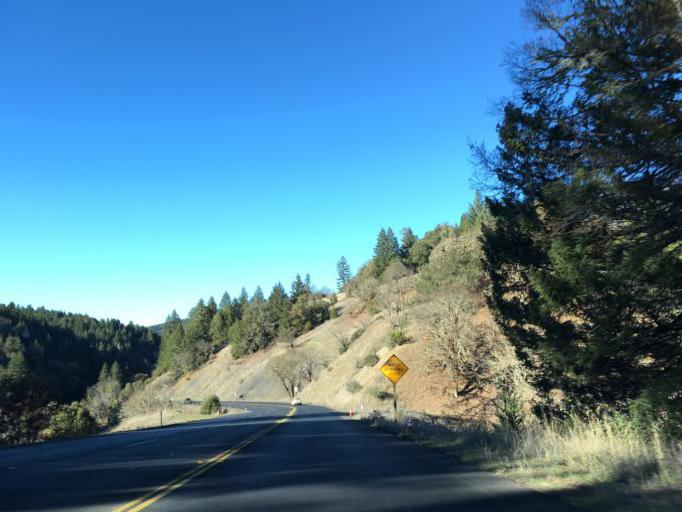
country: US
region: California
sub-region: Mendocino County
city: Laytonville
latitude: 39.7607
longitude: -123.5401
